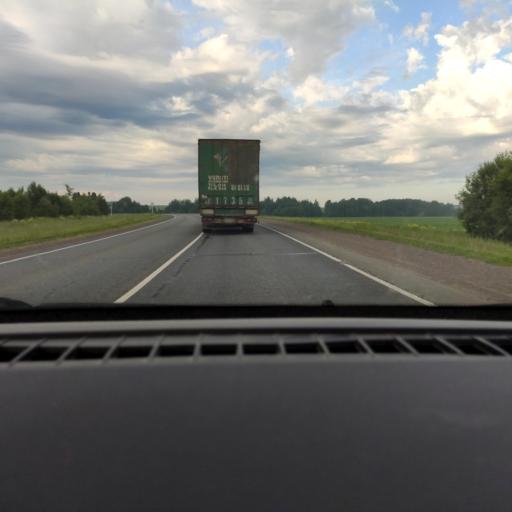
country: RU
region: Perm
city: Chastyye
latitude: 57.3939
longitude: 54.4369
